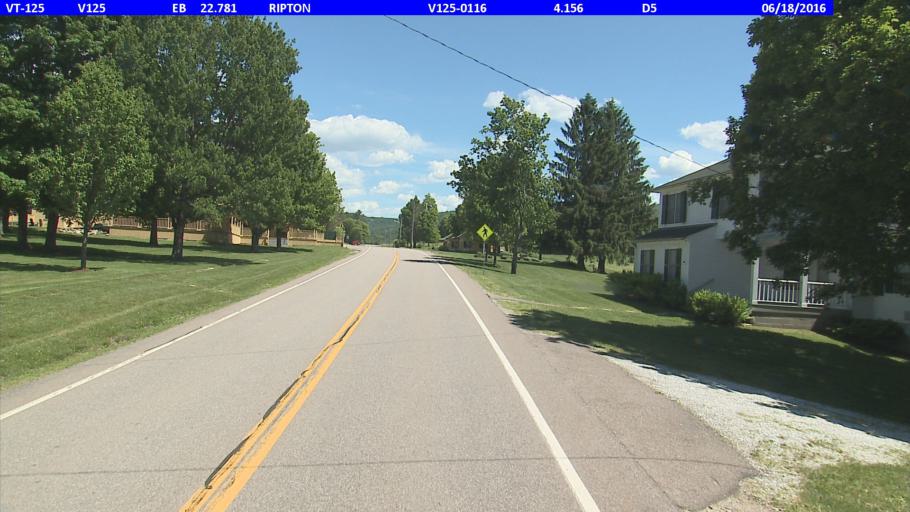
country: US
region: Vermont
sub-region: Rutland County
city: Brandon
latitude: 43.9542
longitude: -72.9945
